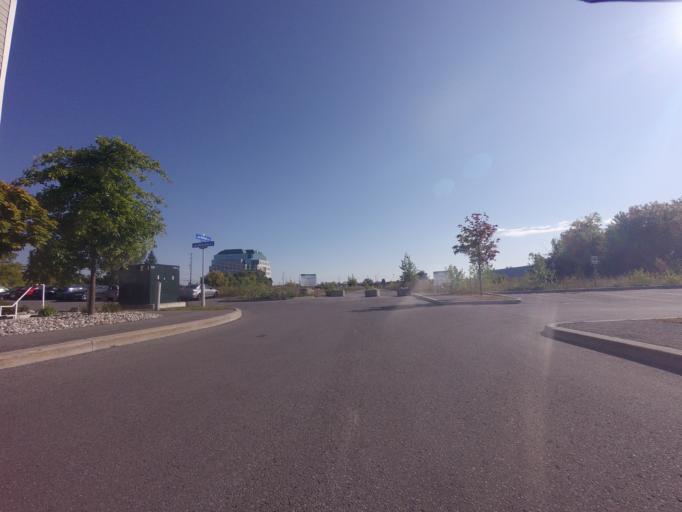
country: CA
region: Ontario
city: Ottawa
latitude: 45.4044
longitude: -75.6298
